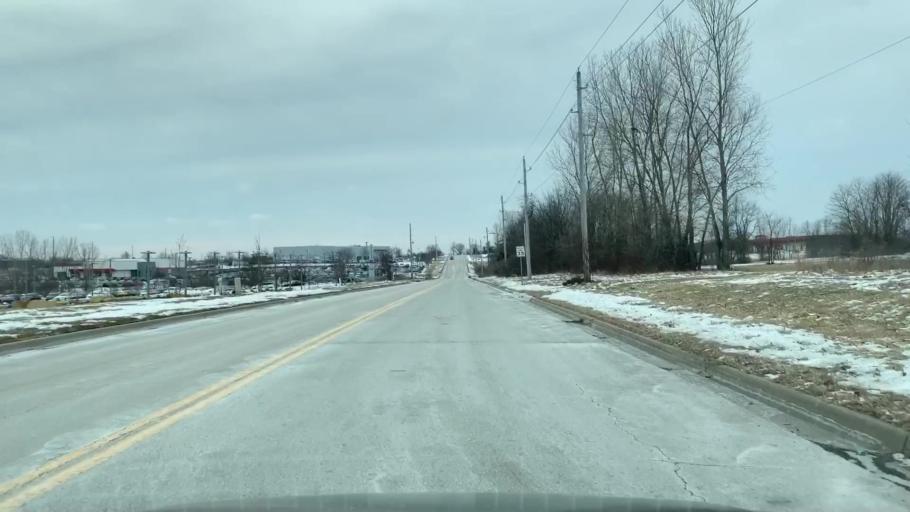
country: US
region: Missouri
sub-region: Jackson County
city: Lees Summit
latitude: 38.9533
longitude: -94.3640
